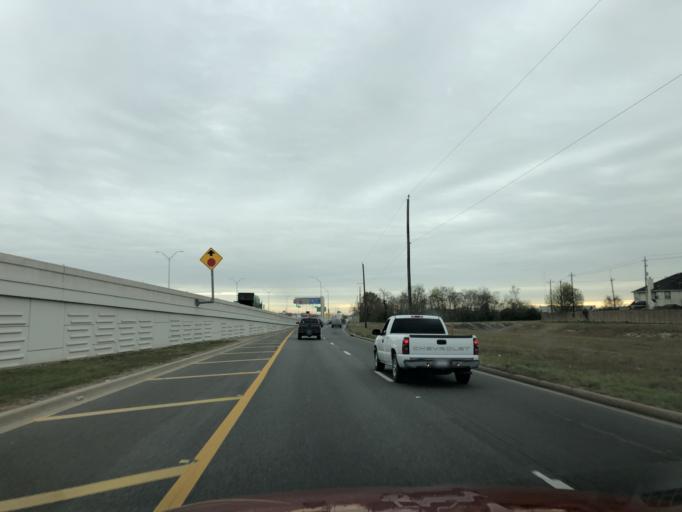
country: US
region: Texas
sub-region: Fort Bend County
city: Missouri City
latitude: 29.6356
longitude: -95.5297
